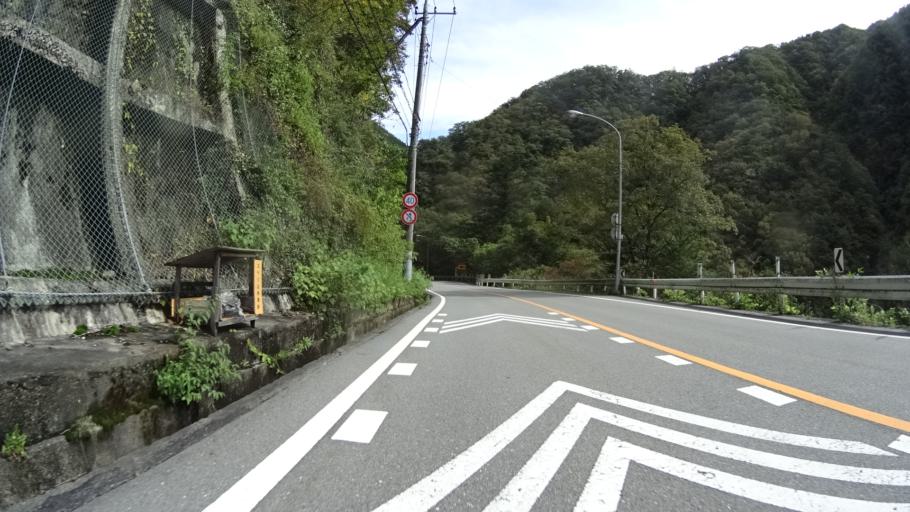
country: JP
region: Yamanashi
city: Otsuki
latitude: 35.7852
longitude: 138.9580
